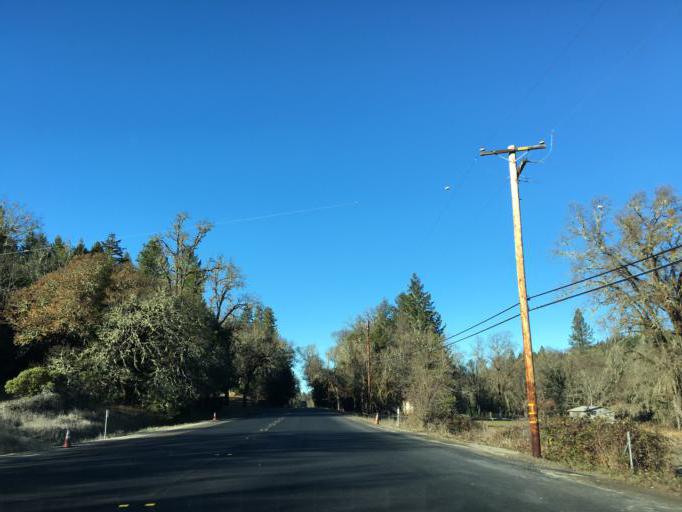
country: US
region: California
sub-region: Mendocino County
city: Laytonville
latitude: 39.6434
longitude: -123.4739
